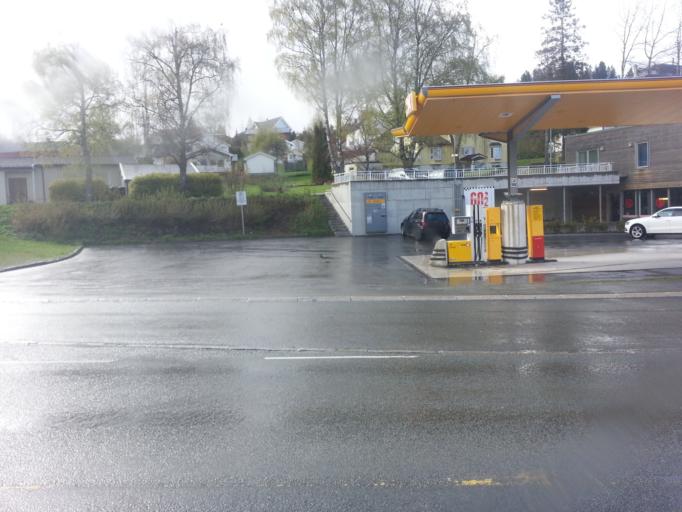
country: NO
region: Sor-Trondelag
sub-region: Trondheim
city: Trondheim
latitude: 63.4019
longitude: 10.3577
